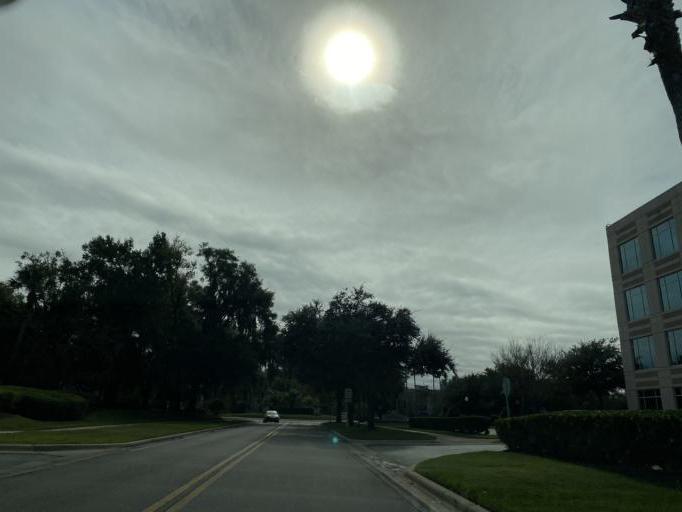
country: US
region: Florida
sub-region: Seminole County
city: Heathrow
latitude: 28.7911
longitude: -81.3543
